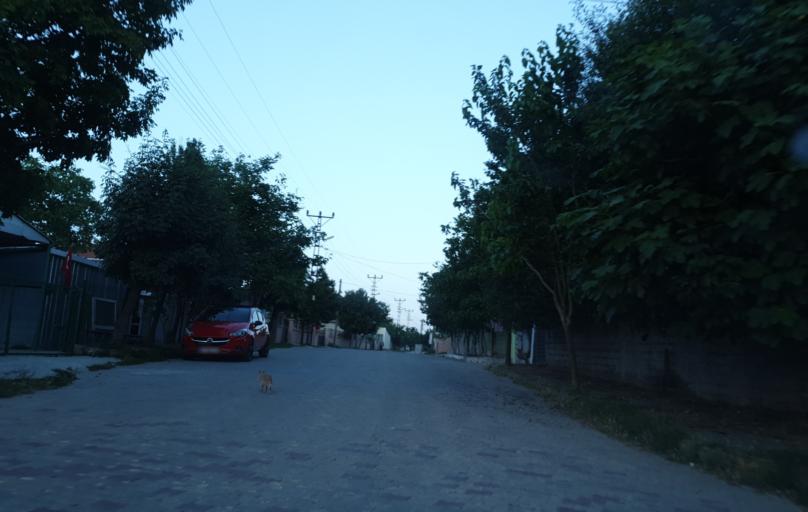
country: TR
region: Tekirdag
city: Velimese
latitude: 41.3492
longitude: 27.8819
